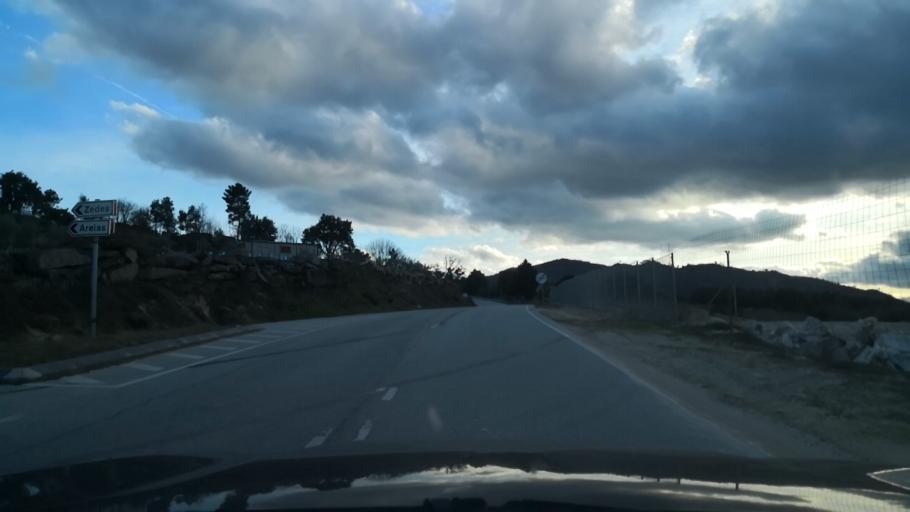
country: PT
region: Braganca
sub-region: Carrazeda de Ansiaes
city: Carrazeda de Anciaes
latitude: 41.2677
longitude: -7.3227
